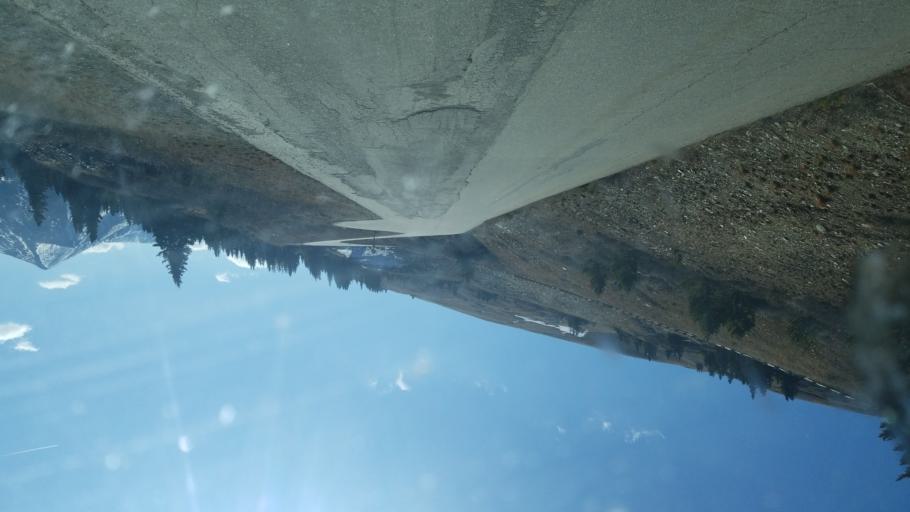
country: US
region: Colorado
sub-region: Chaffee County
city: Buena Vista
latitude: 38.8258
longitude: -106.4050
